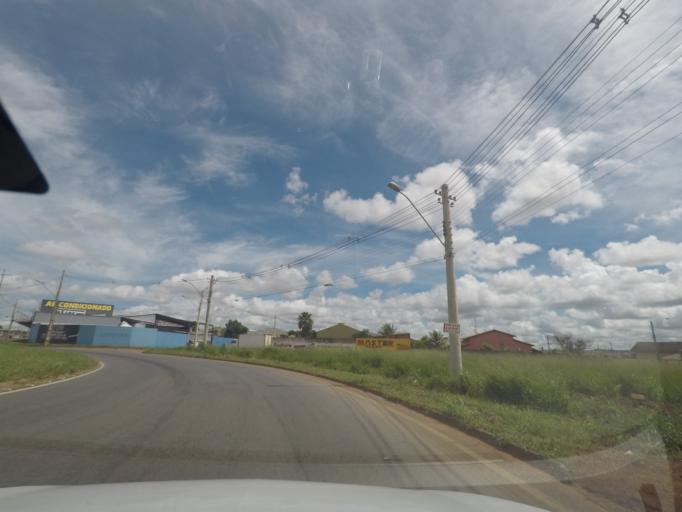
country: BR
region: Goias
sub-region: Goiania
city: Goiania
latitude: -16.7291
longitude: -49.3507
